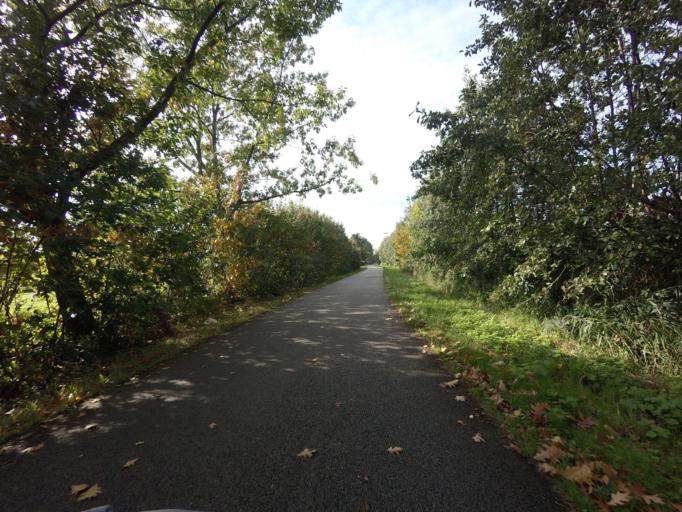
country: NL
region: North Brabant
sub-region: Gemeente Breda
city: Hoge Vucht
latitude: 51.5976
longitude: 4.8174
